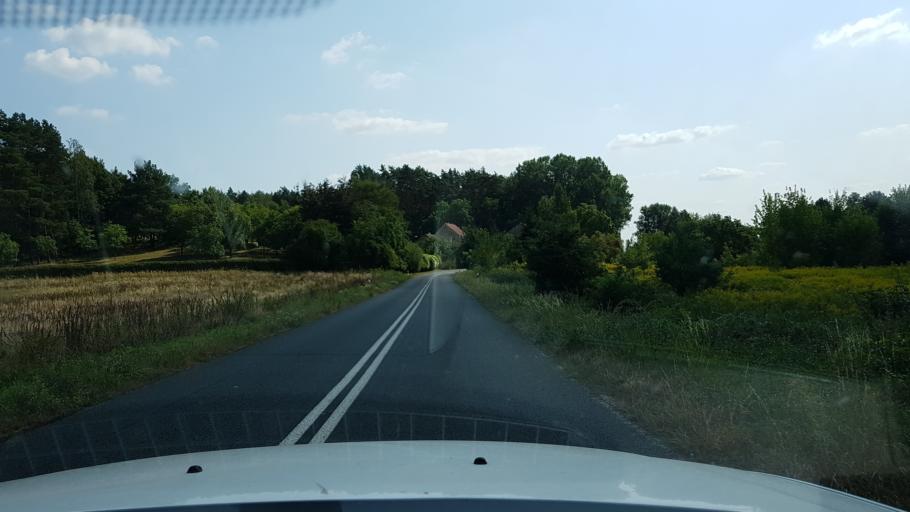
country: PL
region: West Pomeranian Voivodeship
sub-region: Powiat gryfinski
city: Cedynia
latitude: 52.8182
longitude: 14.2366
